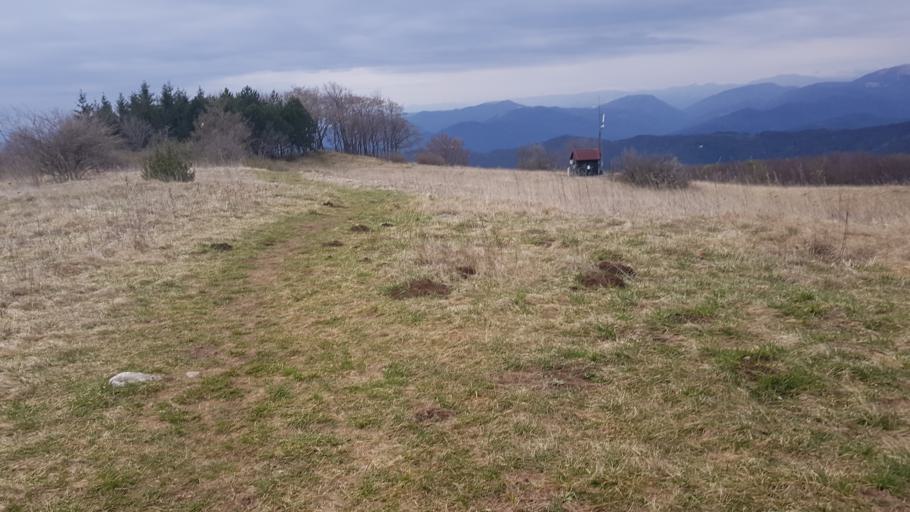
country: SI
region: Kanal
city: Deskle
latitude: 46.0652
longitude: 13.5601
